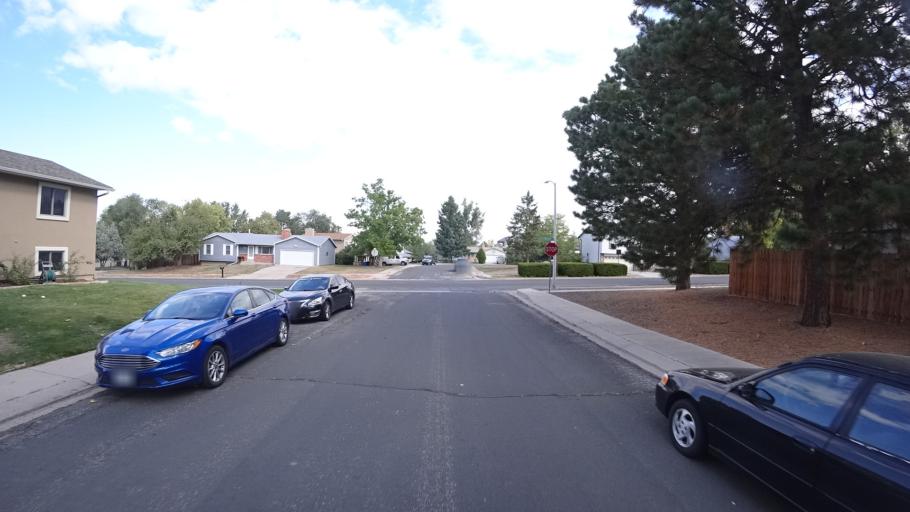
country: US
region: Colorado
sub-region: El Paso County
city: Cimarron Hills
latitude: 38.8835
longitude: -104.7400
